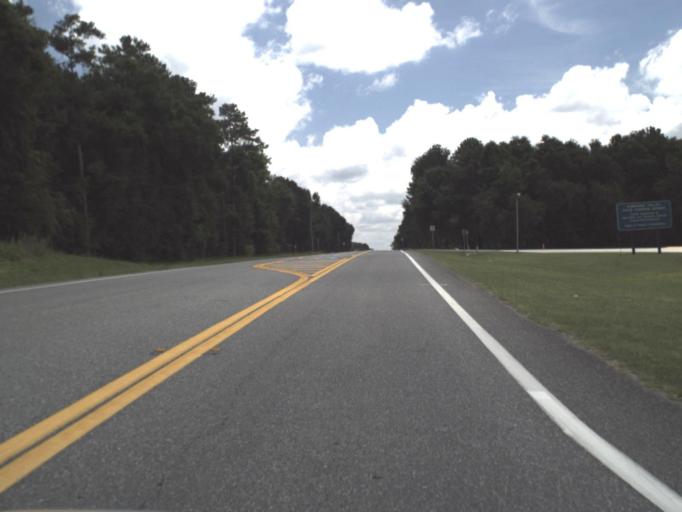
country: US
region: Florida
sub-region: Suwannee County
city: Wellborn
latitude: 30.3202
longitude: -82.8010
